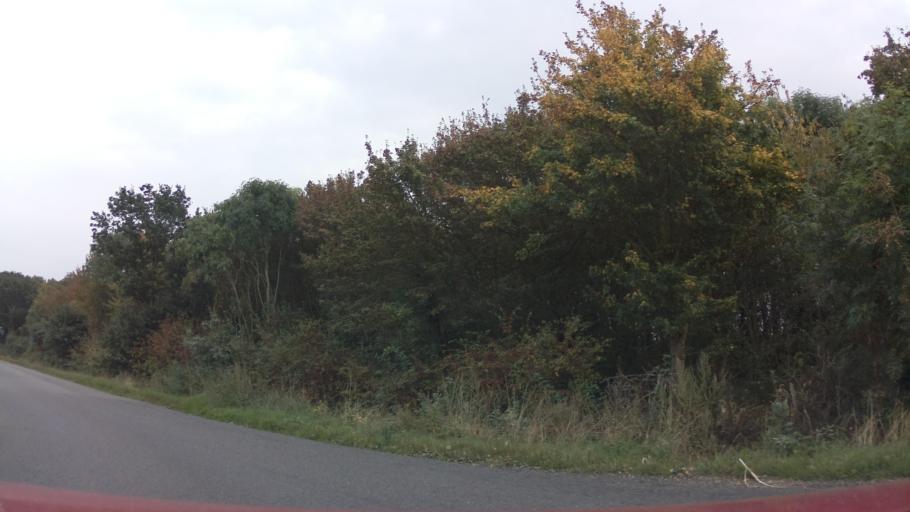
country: GB
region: England
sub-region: Nottinghamshire
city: South Collingham
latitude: 53.1429
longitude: -0.6679
